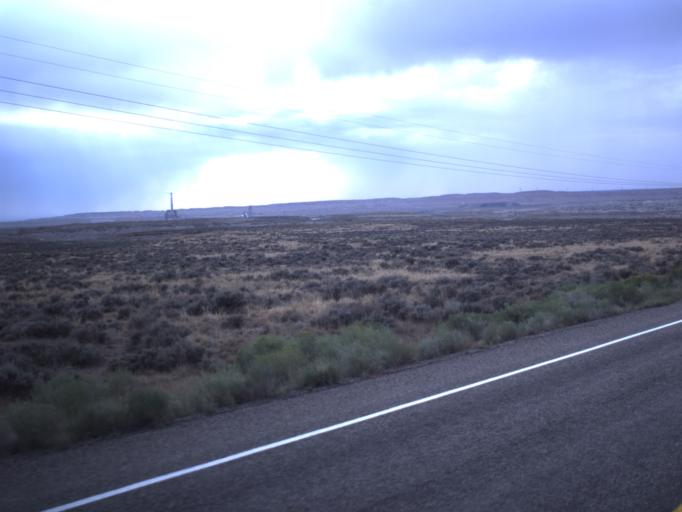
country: US
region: Colorado
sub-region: Rio Blanco County
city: Rangely
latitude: 40.0816
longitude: -109.2137
